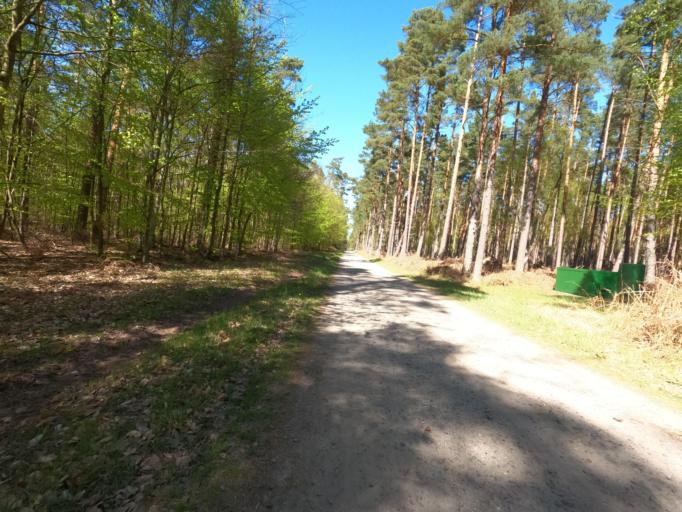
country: DE
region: Mecklenburg-Vorpommern
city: Born
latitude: 54.4069
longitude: 12.5293
